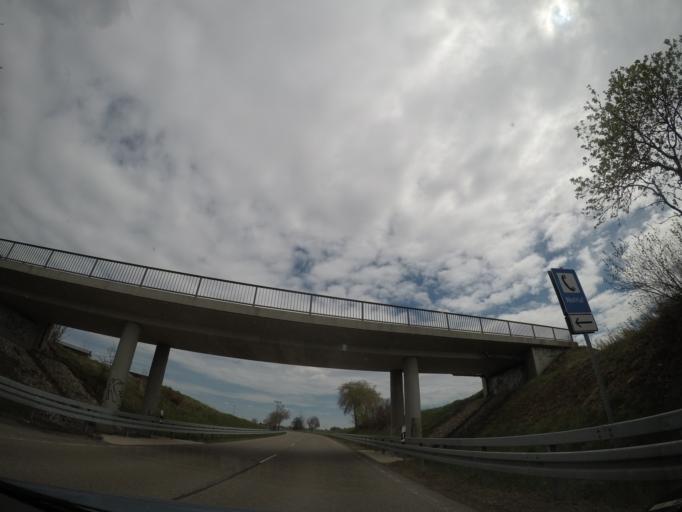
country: DE
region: Baden-Wuerttemberg
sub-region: Tuebingen Region
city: Laichingen
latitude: 48.4555
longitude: 9.7070
